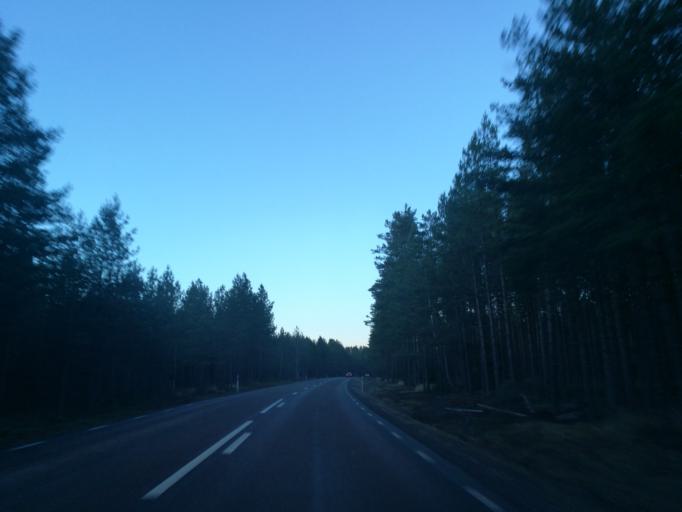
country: SE
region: Vaermland
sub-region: Eda Kommun
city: Charlottenberg
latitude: 59.9043
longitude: 12.2775
